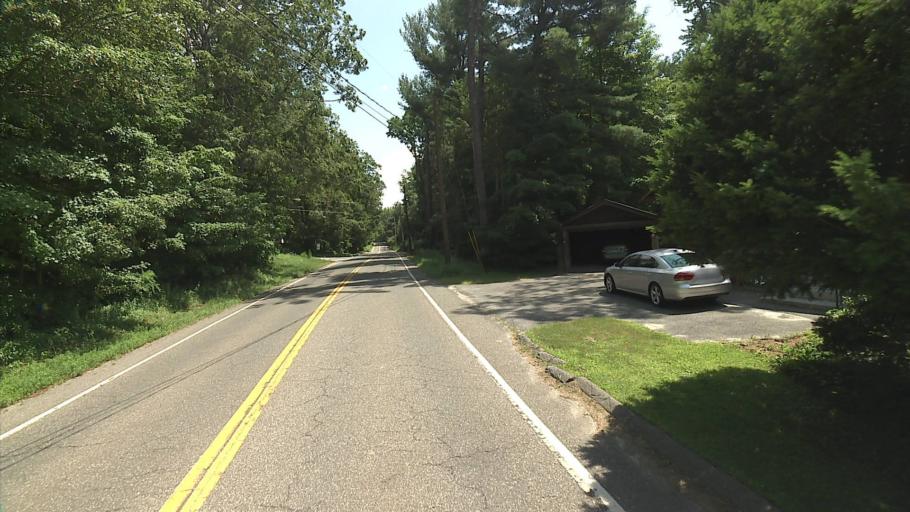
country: US
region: Connecticut
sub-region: Litchfield County
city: Canaan
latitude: 41.8571
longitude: -73.3227
